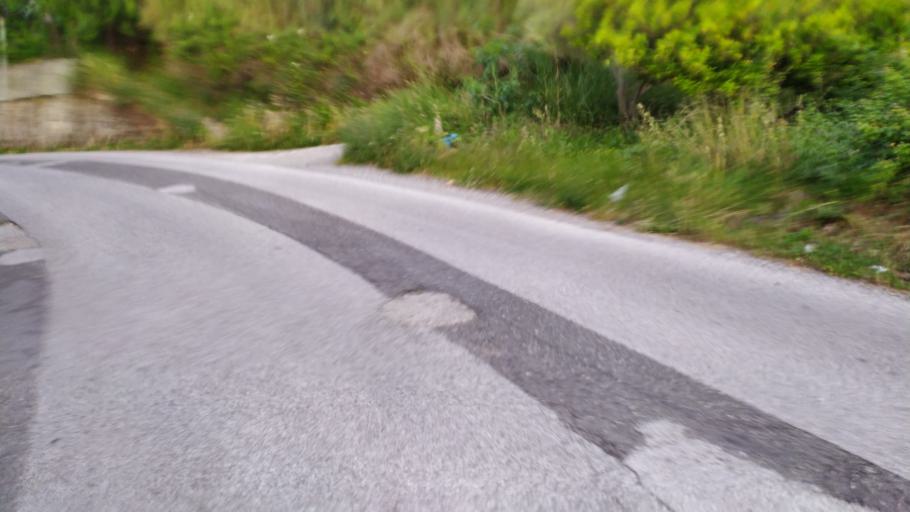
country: IT
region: Sicily
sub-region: Messina
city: Condro
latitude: 38.1677
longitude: 15.3257
